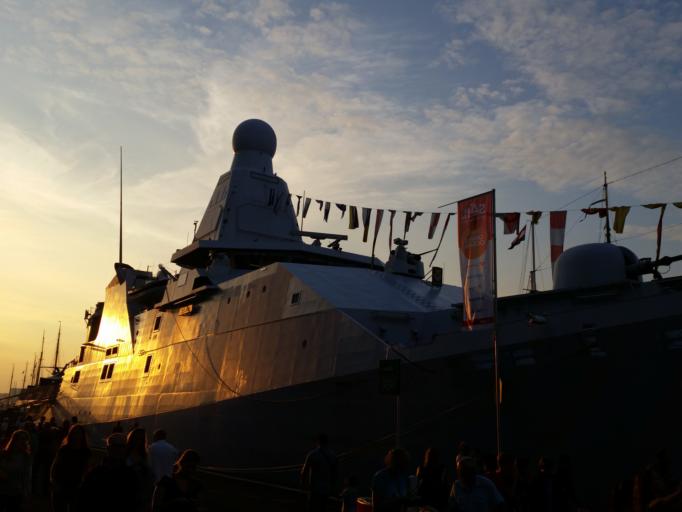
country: NL
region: North Holland
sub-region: Gemeente Amsterdam
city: Amsterdam
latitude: 52.3784
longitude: 4.9153
